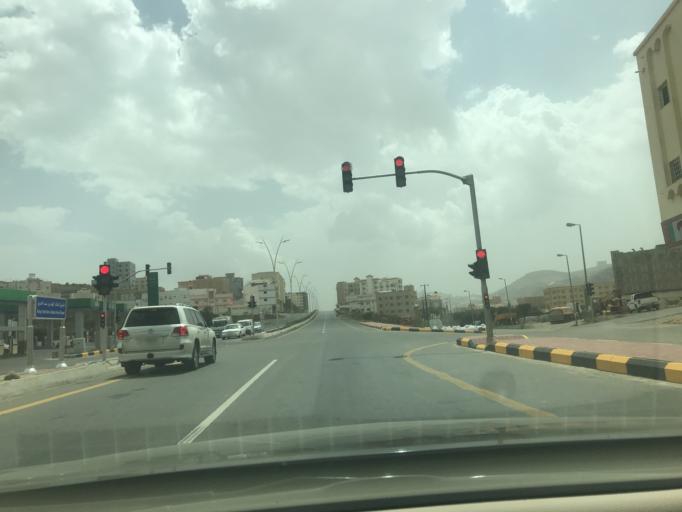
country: SA
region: Mintaqat al Bahah
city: Al Bahah
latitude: 20.0407
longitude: 41.4961
